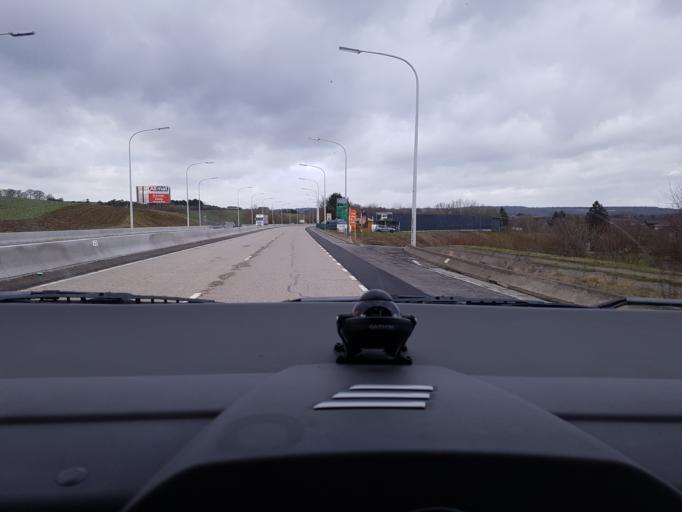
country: BE
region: Wallonia
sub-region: Province du Luxembourg
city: Marche-en-Famenne
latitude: 50.2643
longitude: 5.2530
